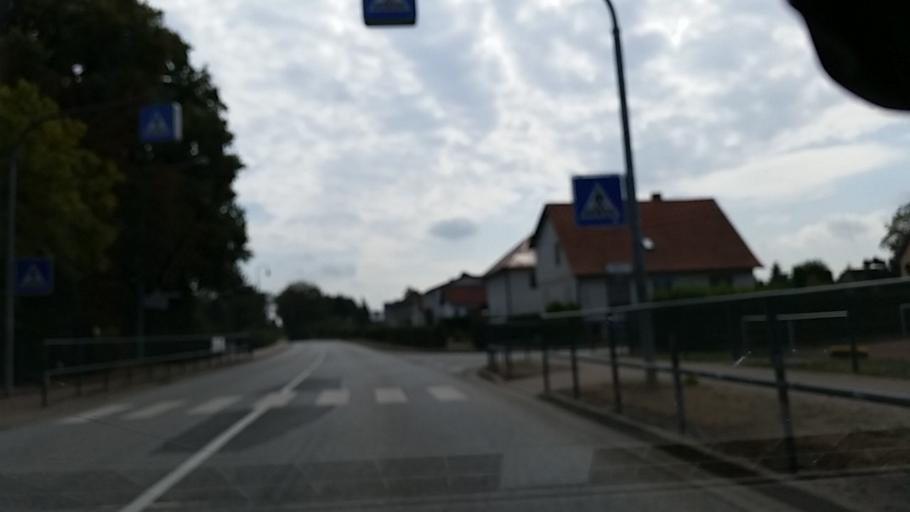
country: DE
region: Saxony-Anhalt
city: Nemsdorf-Gohrendorf
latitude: 51.3439
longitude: 11.6388
